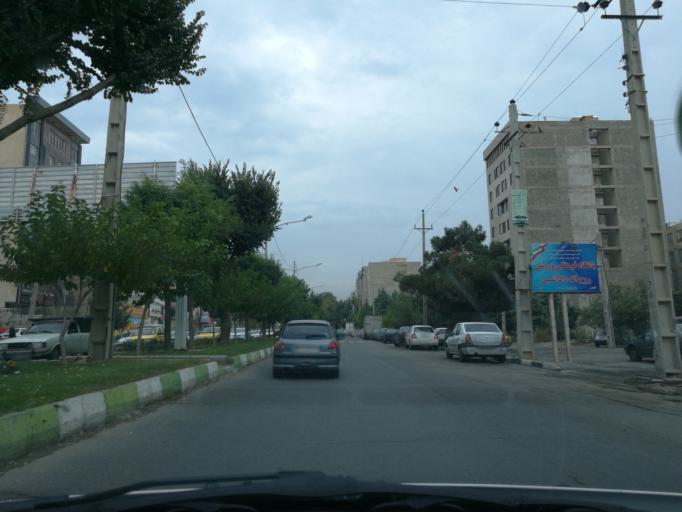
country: IR
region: Alborz
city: Karaj
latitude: 35.8568
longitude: 50.9511
